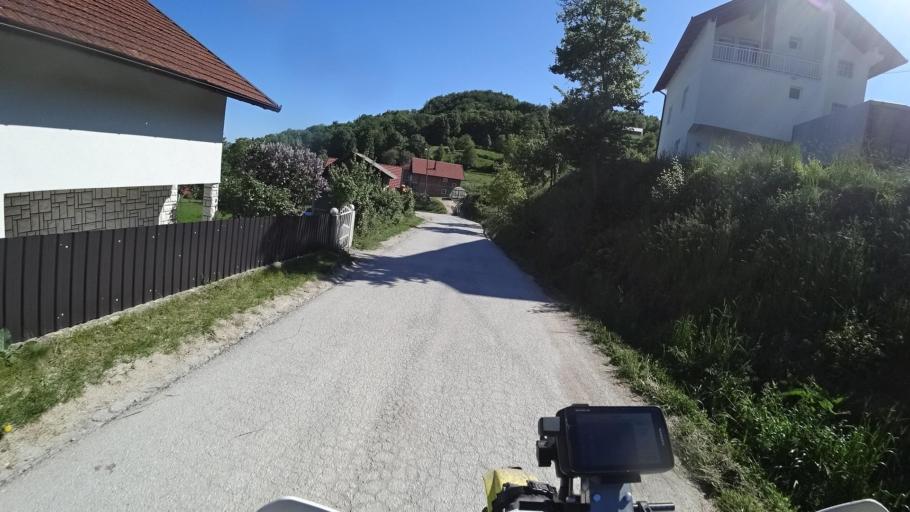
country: BA
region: Federation of Bosnia and Herzegovina
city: Travnik
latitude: 44.2791
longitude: 17.7171
